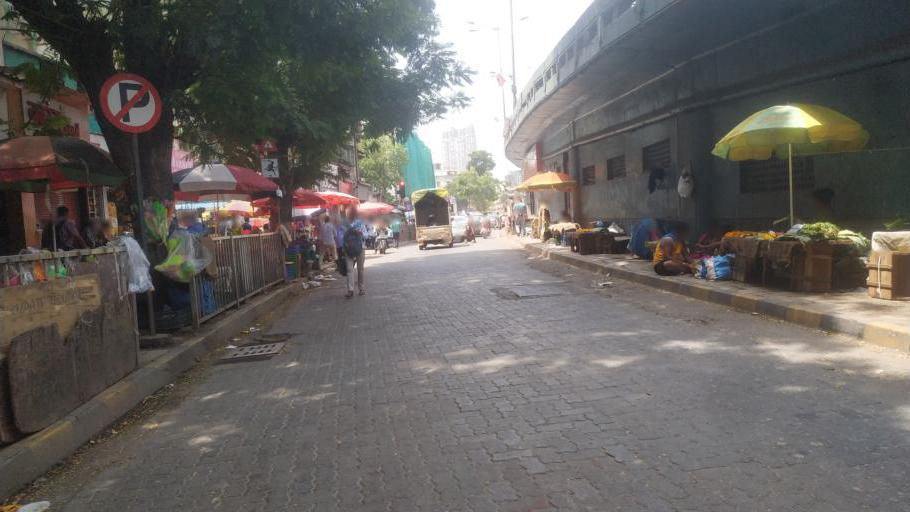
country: IN
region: Maharashtra
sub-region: Mumbai Suburban
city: Mumbai
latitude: 19.0048
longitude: 72.8391
